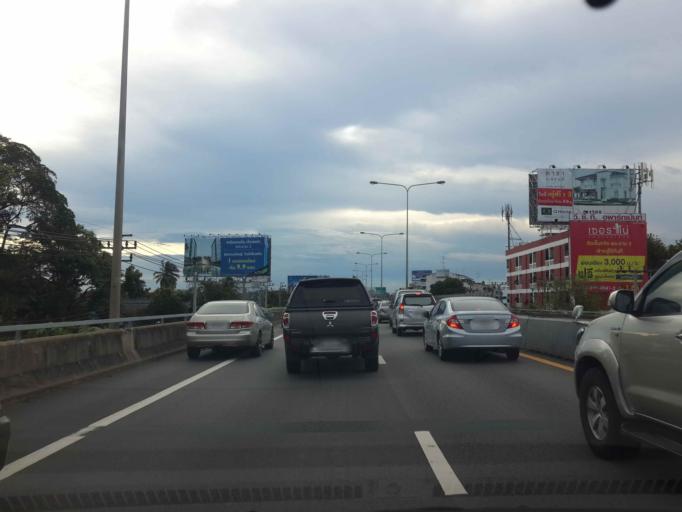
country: TH
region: Bangkok
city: Rat Burana
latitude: 13.6707
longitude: 100.4990
